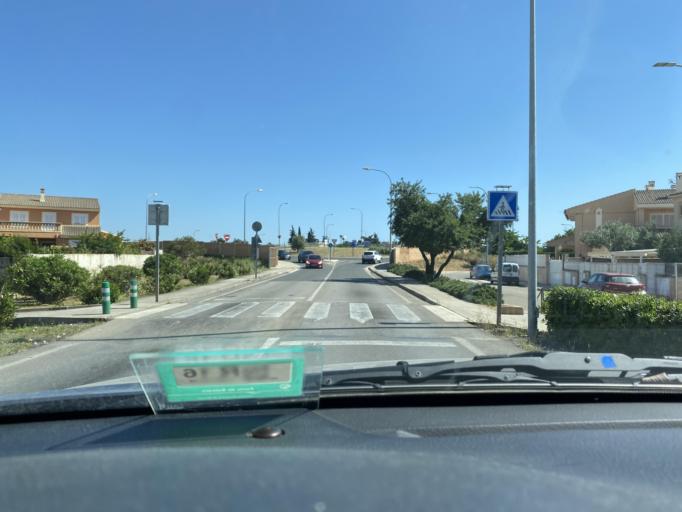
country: ES
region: Balearic Islands
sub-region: Illes Balears
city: Palma
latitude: 39.6080
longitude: 2.6855
